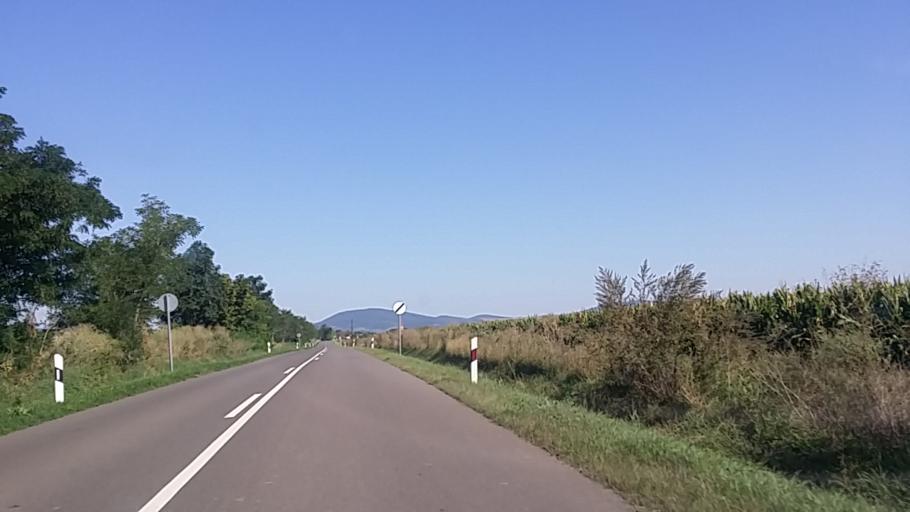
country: HU
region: Nograd
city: Jobbagyi
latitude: 47.8517
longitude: 19.6293
